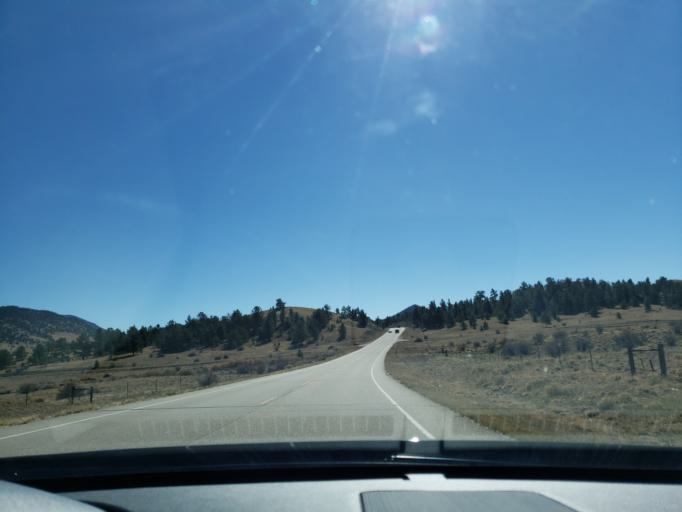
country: US
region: Colorado
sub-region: Chaffee County
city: Buena Vista
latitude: 38.8717
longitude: -105.6689
